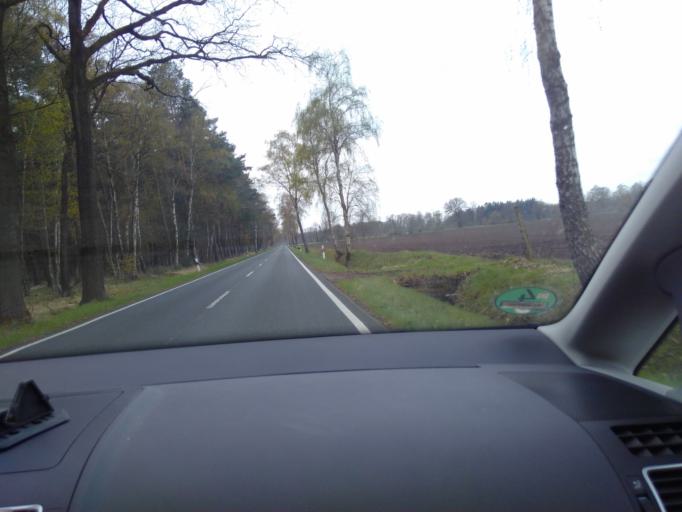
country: DE
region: Lower Saxony
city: Adelheidsdorf
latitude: 52.5821
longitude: 10.0276
